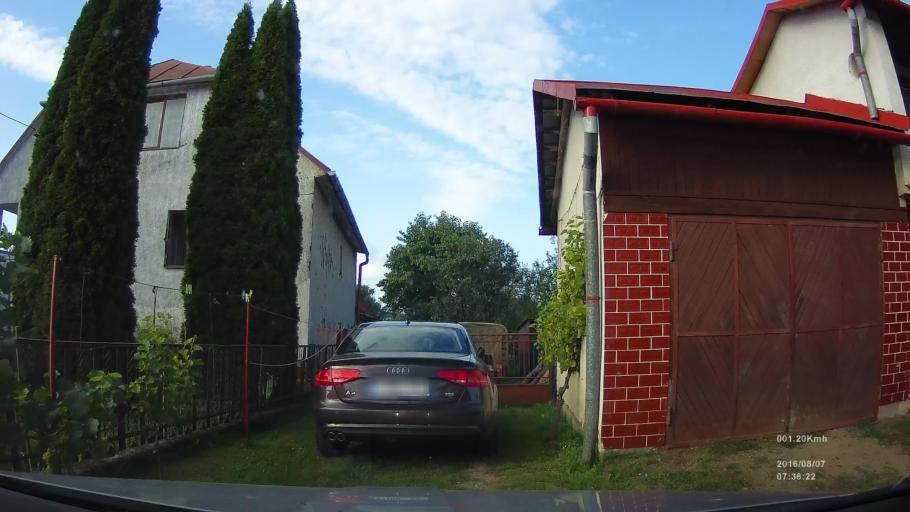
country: SK
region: Presovsky
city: Stropkov
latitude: 49.2282
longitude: 21.6618
